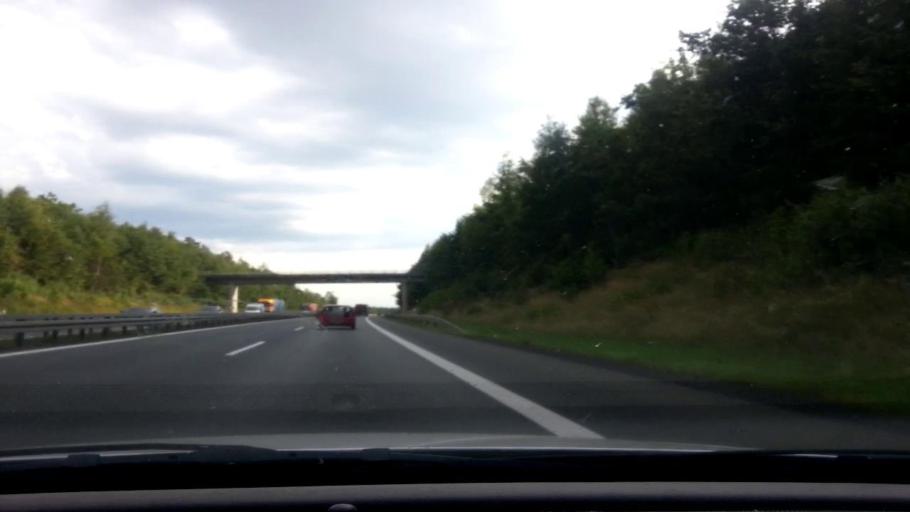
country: DE
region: Bavaria
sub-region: Upper Palatinate
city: Wiesau
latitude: 49.8956
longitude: 12.2195
